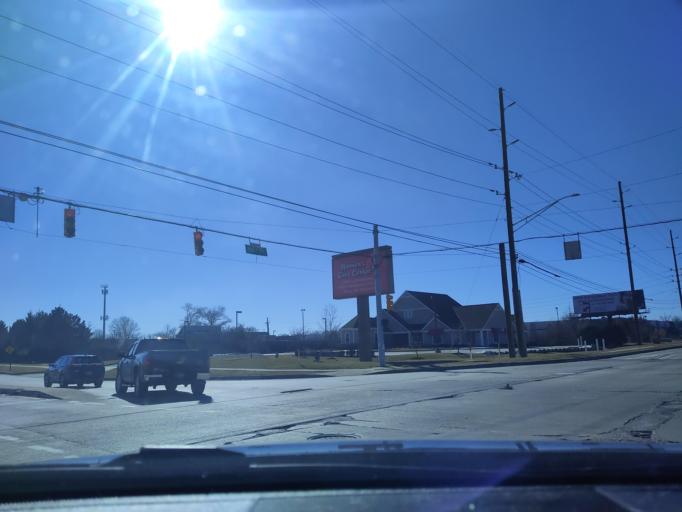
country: US
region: Indiana
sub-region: Boone County
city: Zionsville
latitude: 39.9114
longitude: -86.2408
